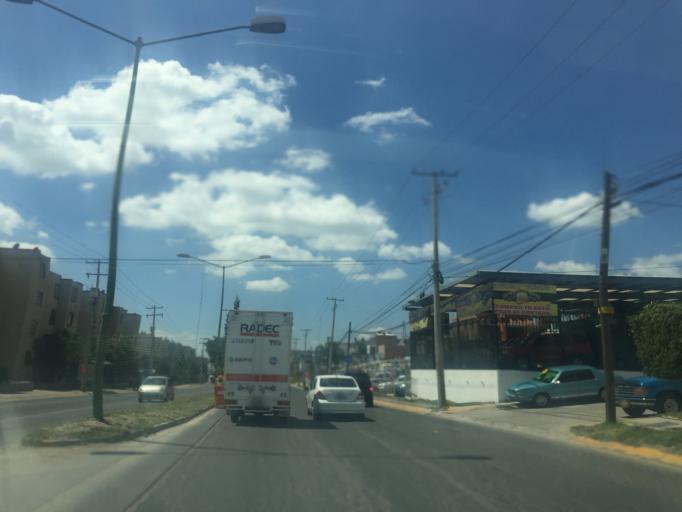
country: MX
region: Guanajuato
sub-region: Leon
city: Ejido la Joya
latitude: 21.1318
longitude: -101.7171
